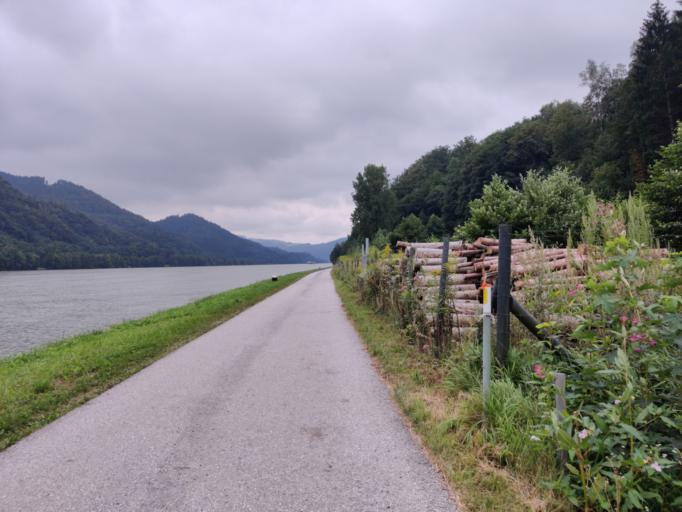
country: AT
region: Lower Austria
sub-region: Politischer Bezirk Melk
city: Nochling
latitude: 48.2251
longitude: 14.9434
